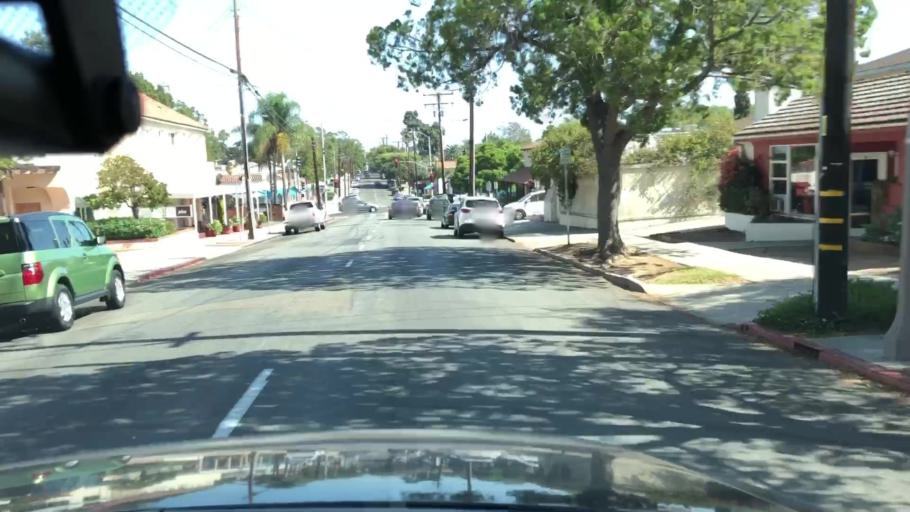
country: US
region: California
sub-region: Santa Barbara County
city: Santa Barbara
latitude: 34.4293
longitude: -119.7178
